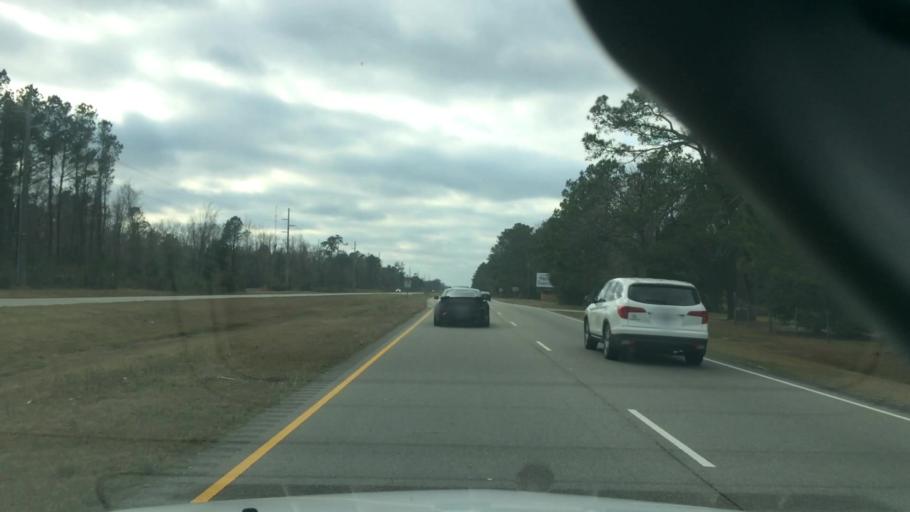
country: US
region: North Carolina
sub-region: Brunswick County
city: Shallotte
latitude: 34.0055
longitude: -78.3067
